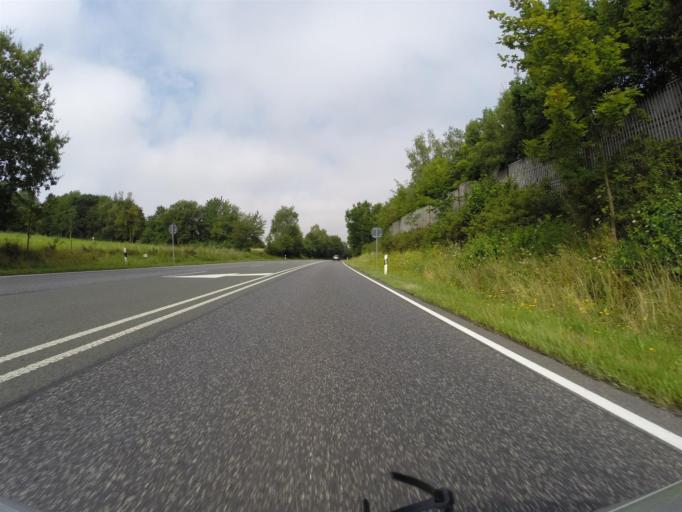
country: DE
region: Hesse
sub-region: Regierungsbezirk Kassel
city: Kaufungen
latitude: 51.2744
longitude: 9.6328
